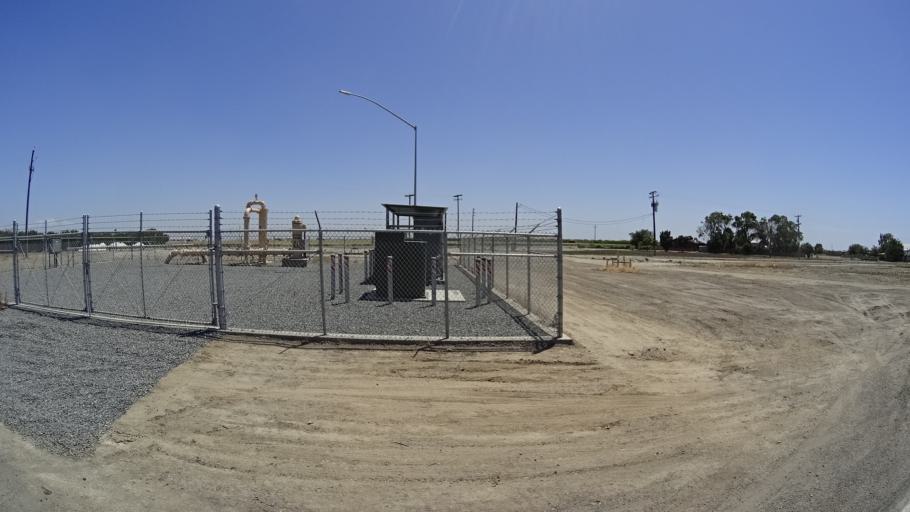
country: US
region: California
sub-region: Kings County
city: Corcoran
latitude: 36.1201
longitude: -119.5371
